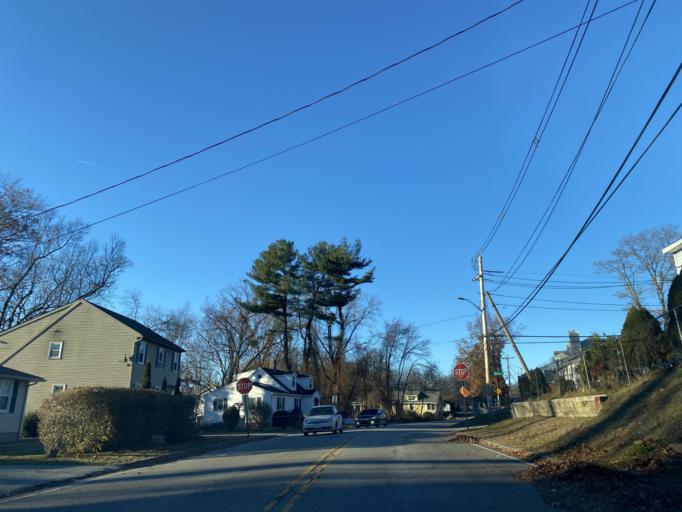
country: US
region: Massachusetts
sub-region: Worcester County
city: Hamilton
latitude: 42.2517
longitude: -71.7621
